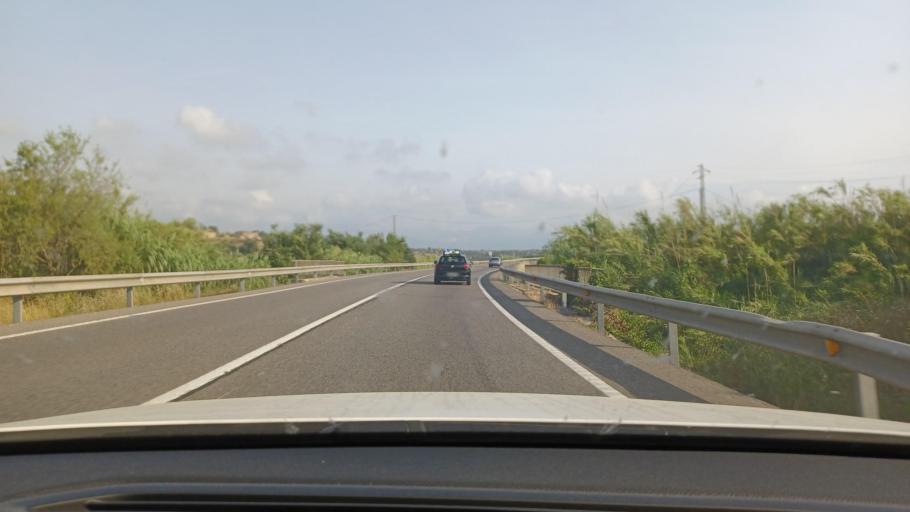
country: ES
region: Catalonia
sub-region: Provincia de Tarragona
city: Tortosa
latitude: 40.7878
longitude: 0.4967
